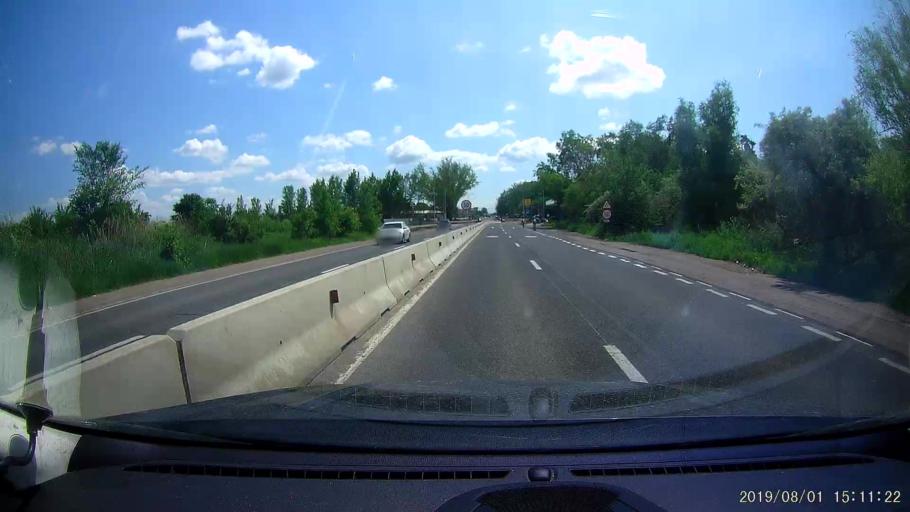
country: RO
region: Braila
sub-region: Comuna Chiscani
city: Chiscani
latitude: 45.2178
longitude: 27.9241
